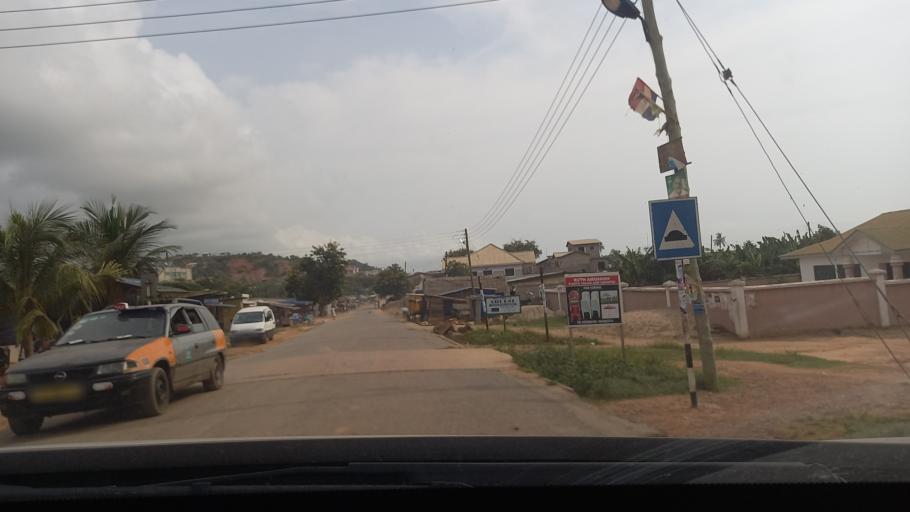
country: GH
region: Western
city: Shama Junction
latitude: 4.9778
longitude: -1.6445
